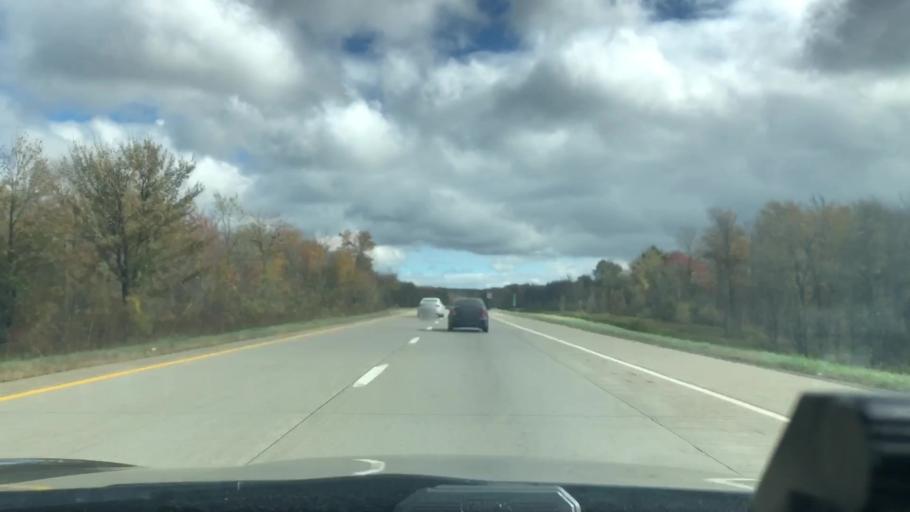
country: US
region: Pennsylvania
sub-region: Lackawanna County
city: Moscow
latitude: 41.2260
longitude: -75.4913
